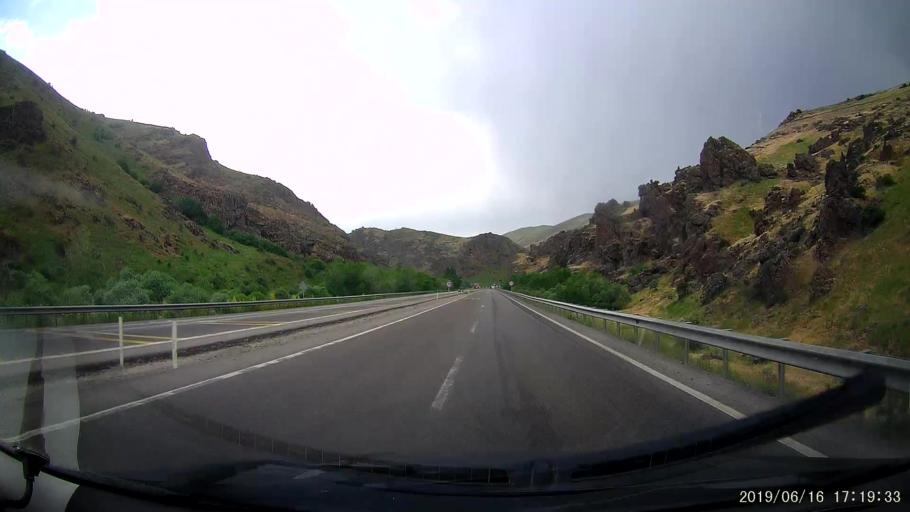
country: TR
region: Erzincan
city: Tercan
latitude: 39.8005
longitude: 40.5274
